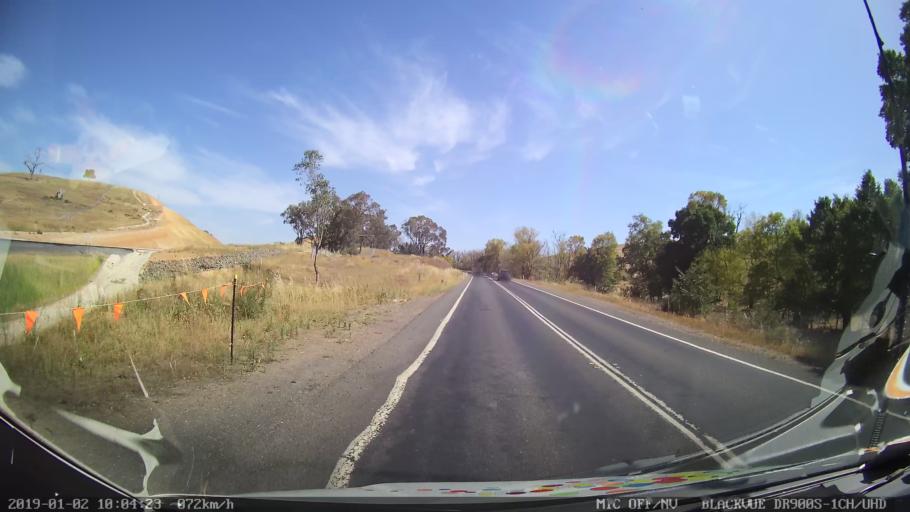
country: AU
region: New South Wales
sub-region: Gundagai
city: Gundagai
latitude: -35.1683
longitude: 148.1232
